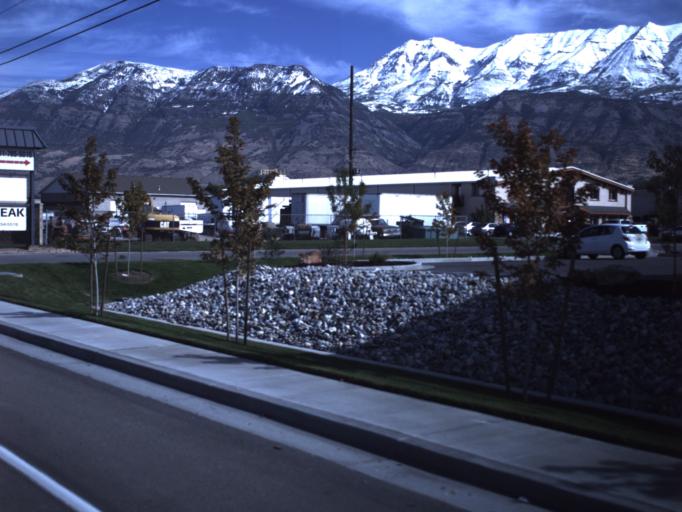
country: US
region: Utah
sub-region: Utah County
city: Lindon
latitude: 40.3400
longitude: -111.7398
